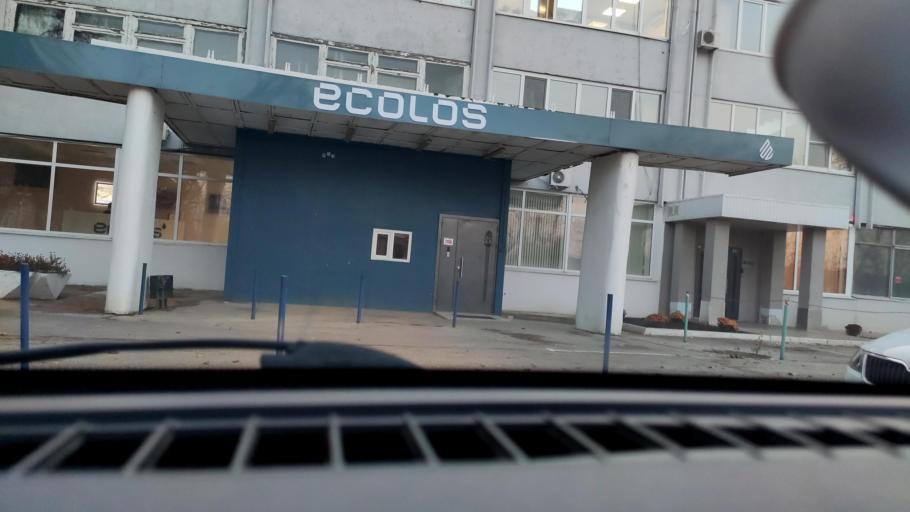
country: RU
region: Samara
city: Samara
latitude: 53.1797
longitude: 50.1145
